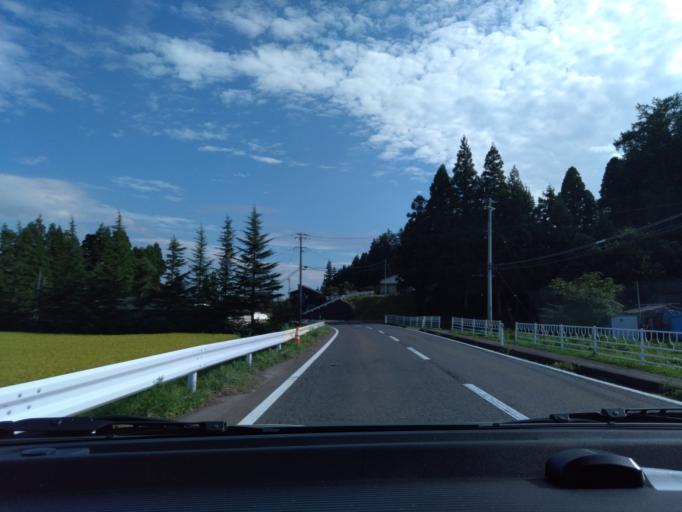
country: JP
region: Iwate
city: Hanamaki
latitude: 39.5335
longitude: 141.1122
